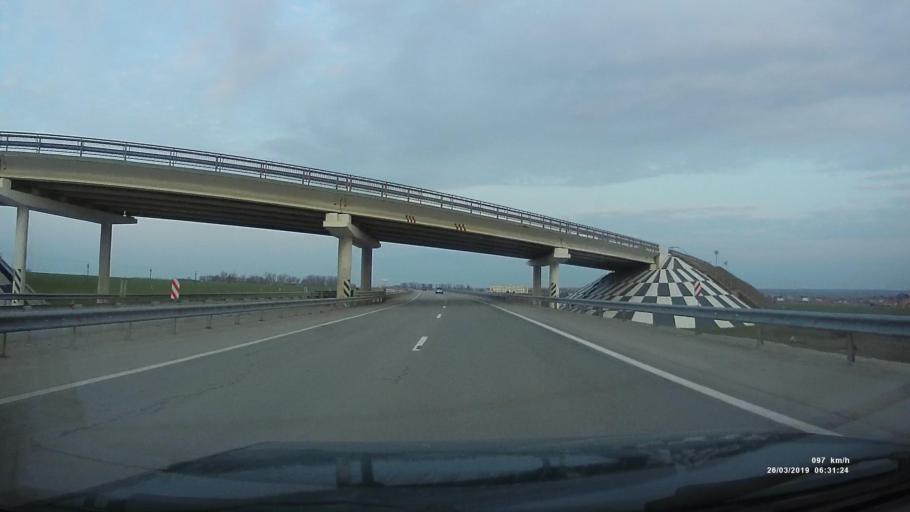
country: RU
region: Rostov
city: Krym
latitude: 47.2732
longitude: 39.5324
